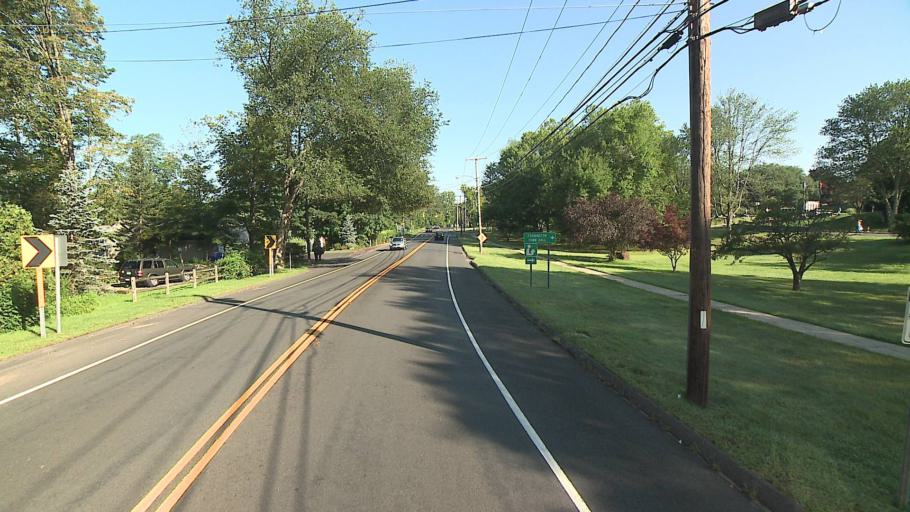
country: US
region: Connecticut
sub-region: Hartford County
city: Farmington
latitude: 41.7475
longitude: -72.8677
